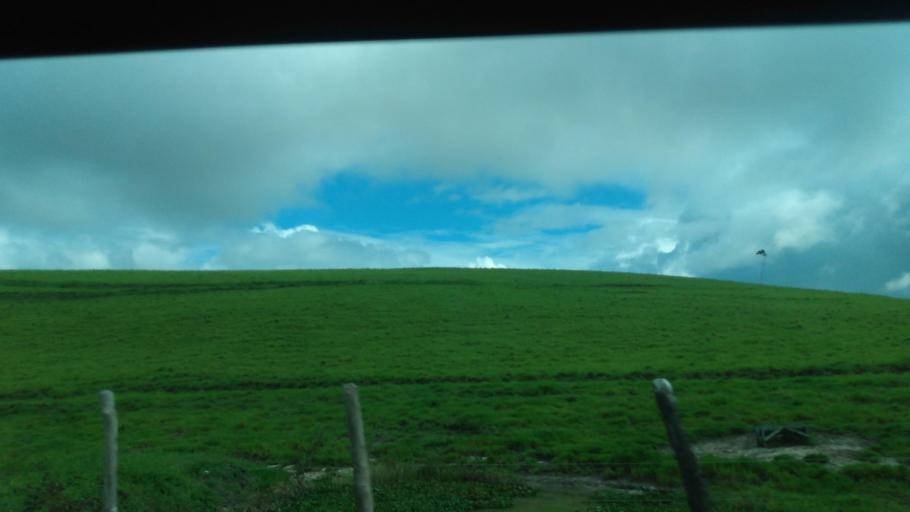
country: BR
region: Pernambuco
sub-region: Quipapa
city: Quipapa
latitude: -8.7765
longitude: -35.9274
